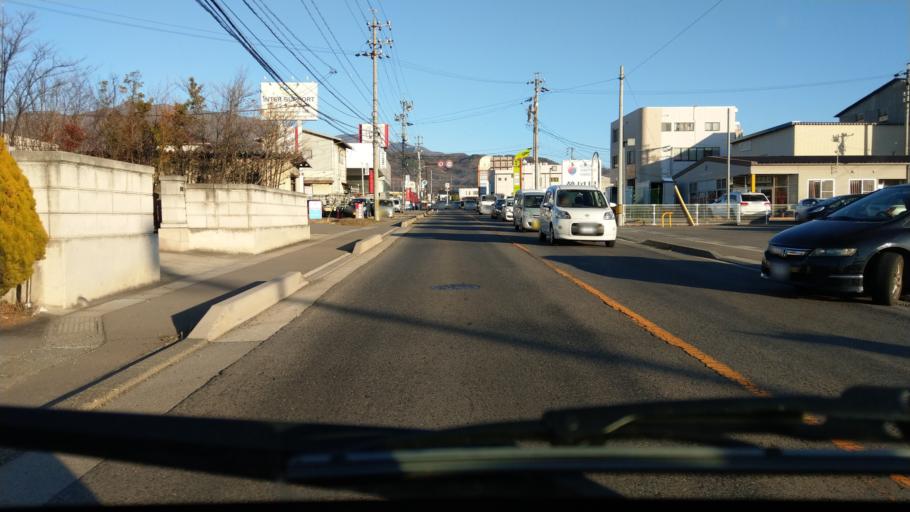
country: JP
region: Nagano
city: Ueda
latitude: 36.4016
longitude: 138.2830
